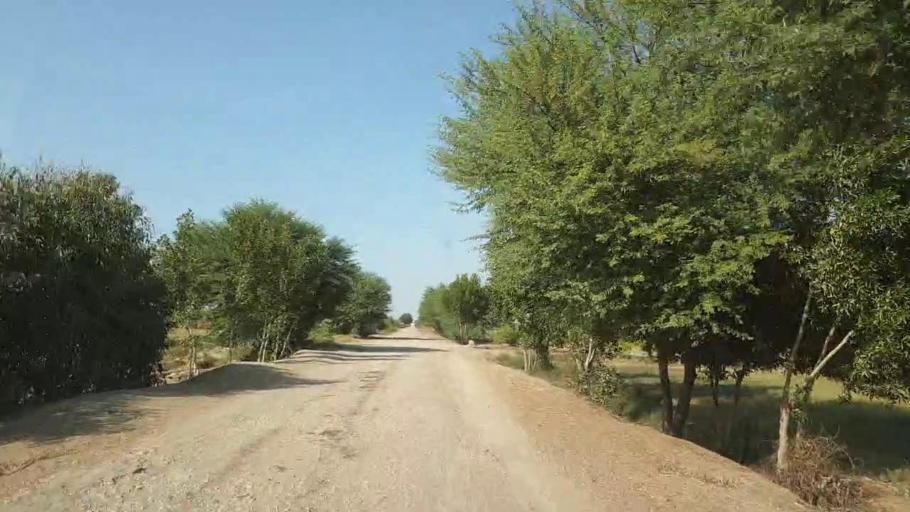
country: PK
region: Sindh
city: Nabisar
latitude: 25.0253
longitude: 69.4865
